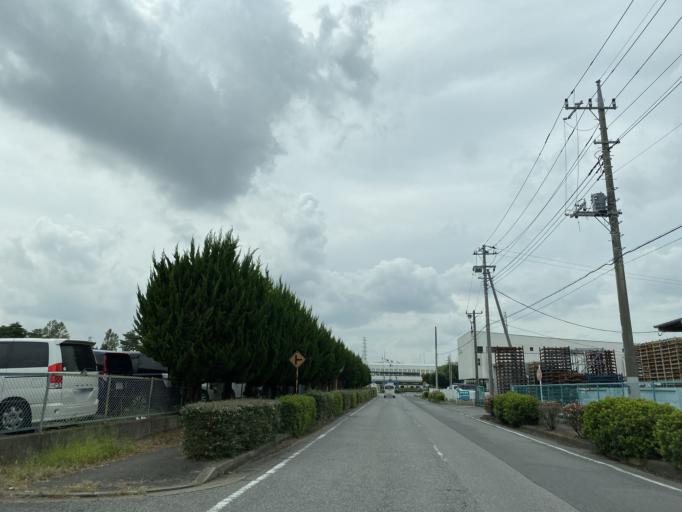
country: JP
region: Ibaraki
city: Mitsukaido
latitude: 36.0273
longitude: 140.0462
